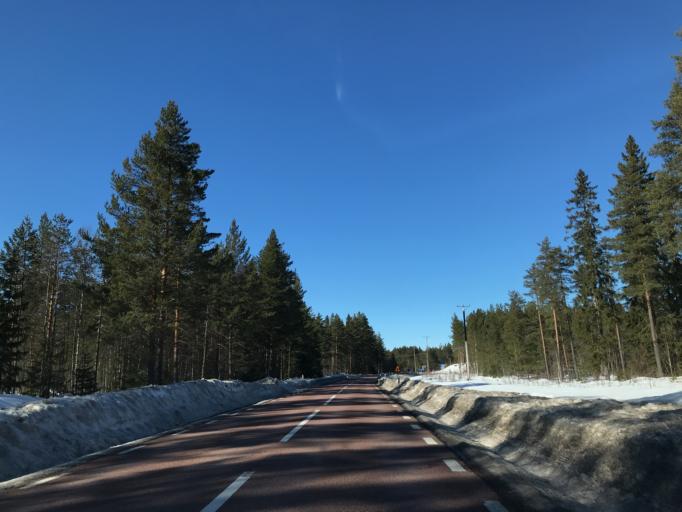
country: SE
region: Dalarna
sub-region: Vansbro Kommun
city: Vansbro
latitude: 60.2493
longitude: 14.1766
